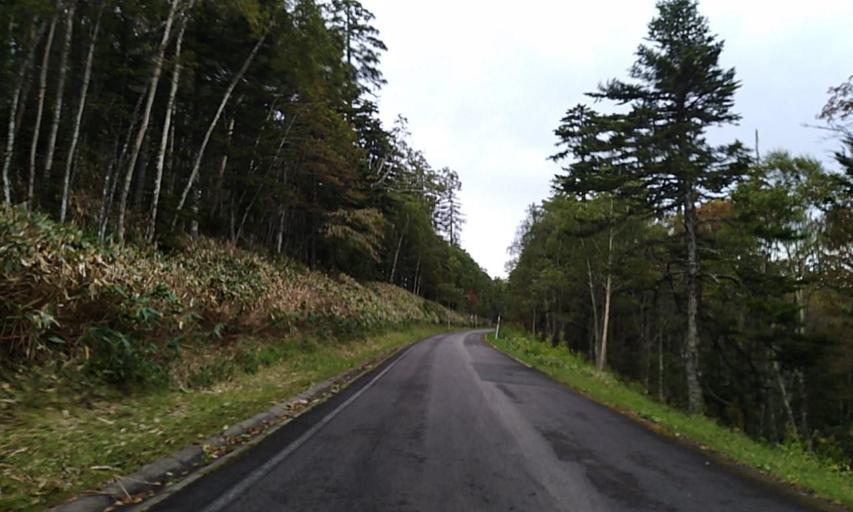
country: JP
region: Hokkaido
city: Bihoro
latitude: 43.5729
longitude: 144.2264
